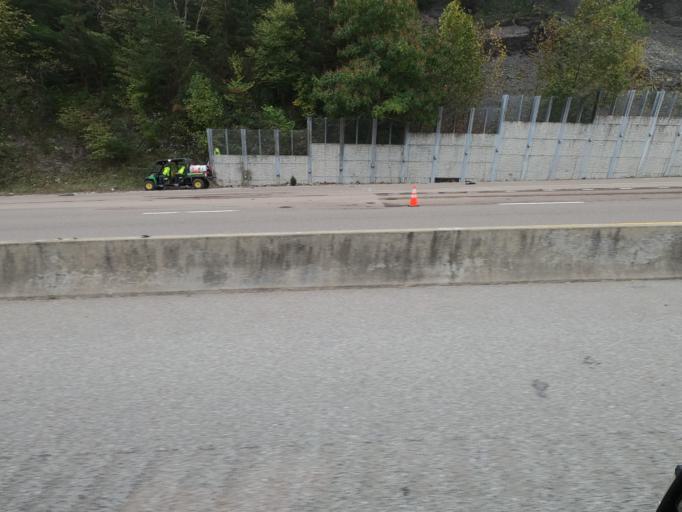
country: US
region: Tennessee
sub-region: Campbell County
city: Jellico
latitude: 36.5413
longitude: -84.1592
